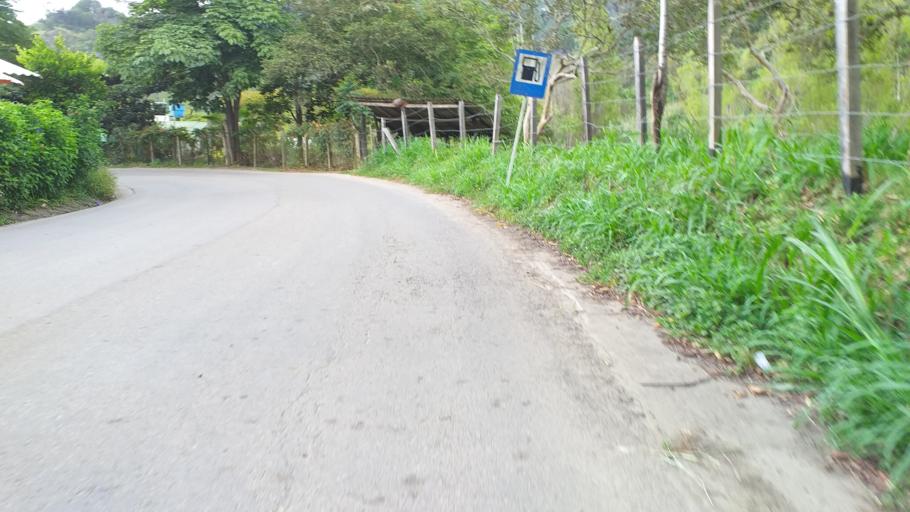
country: CO
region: Cundinamarca
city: Tenza
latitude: 5.0895
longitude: -73.4420
